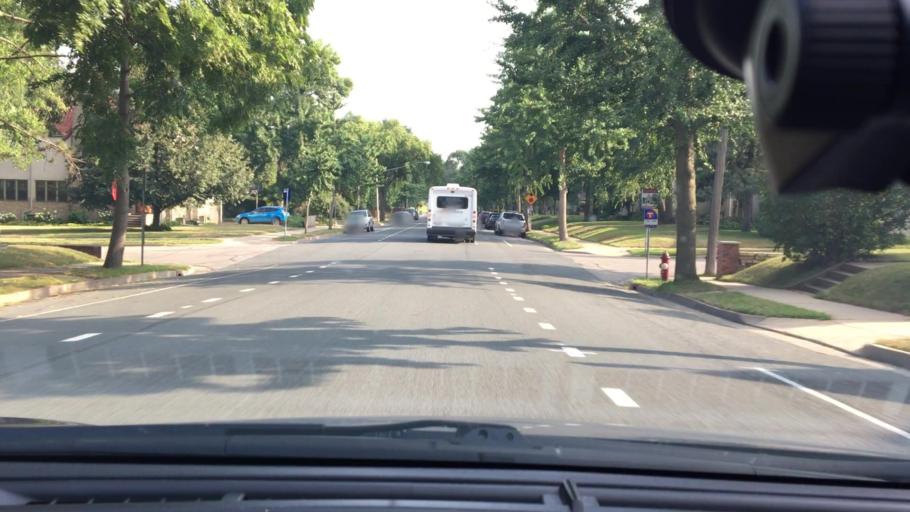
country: US
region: Minnesota
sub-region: Hennepin County
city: Richfield
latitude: 44.9074
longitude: -93.2525
